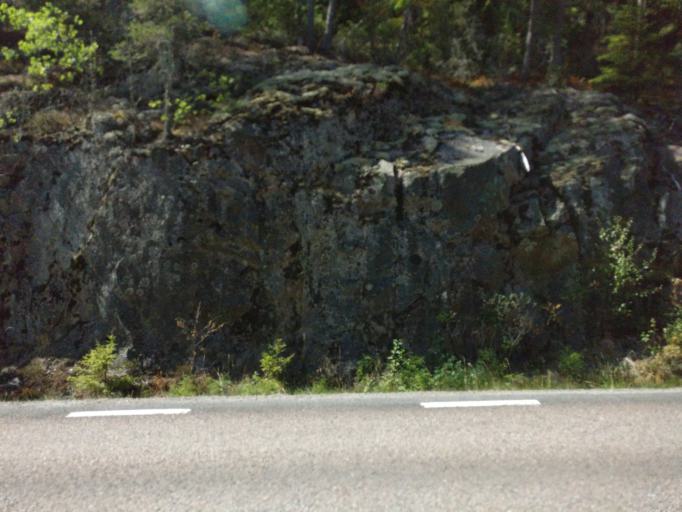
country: SE
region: Vaermland
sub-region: Hagfors Kommun
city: Ekshaerad
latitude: 60.0868
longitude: 13.5544
